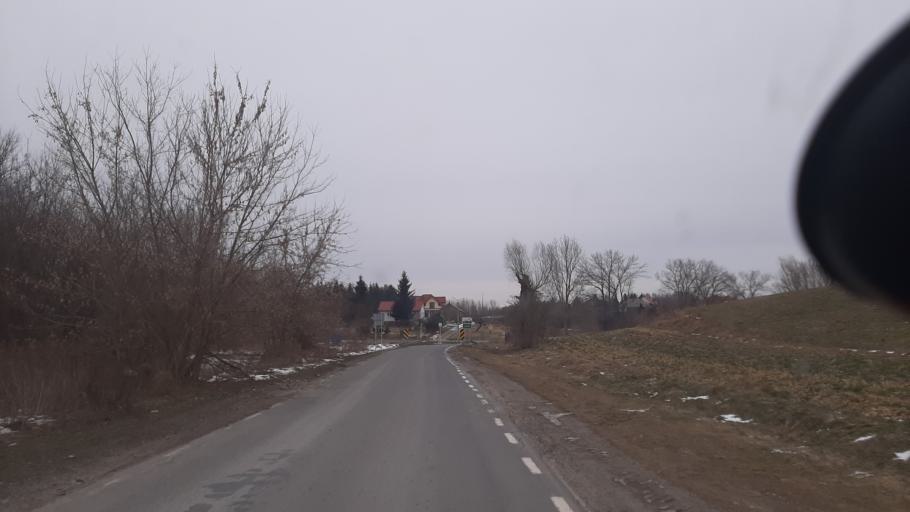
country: PL
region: Lublin Voivodeship
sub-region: Powiat lubelski
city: Jakubowice Murowane
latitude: 51.2799
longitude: 22.6036
